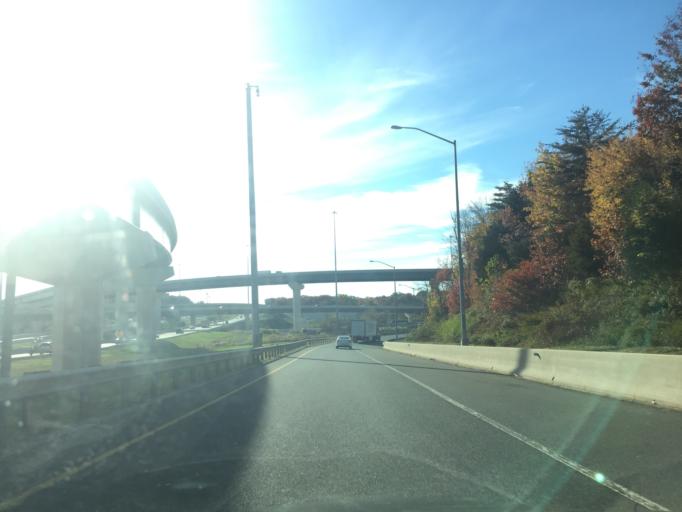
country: US
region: Maryland
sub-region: Baltimore County
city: Rossville
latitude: 39.3537
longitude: -76.4938
